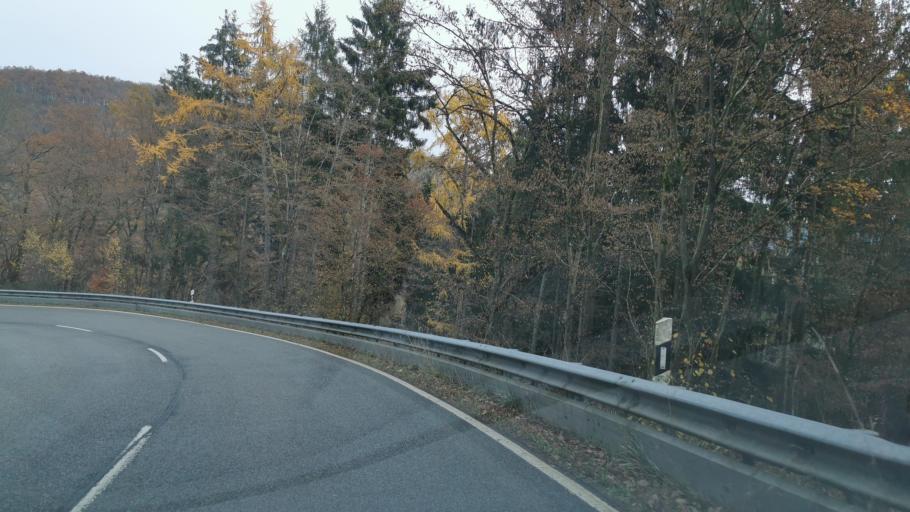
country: DE
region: Rheinland-Pfalz
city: Leienkaul
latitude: 50.1959
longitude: 7.0918
